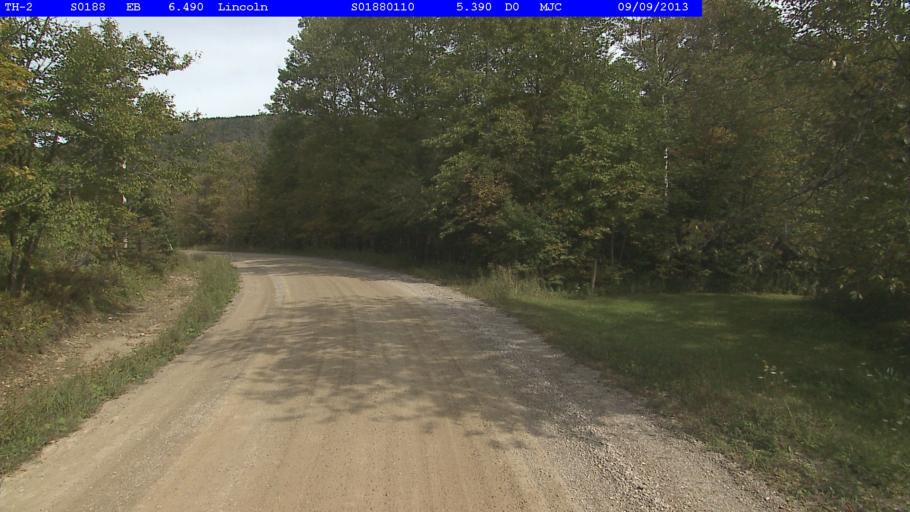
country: US
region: Vermont
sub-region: Addison County
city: Bristol
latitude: 44.0882
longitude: -72.9478
